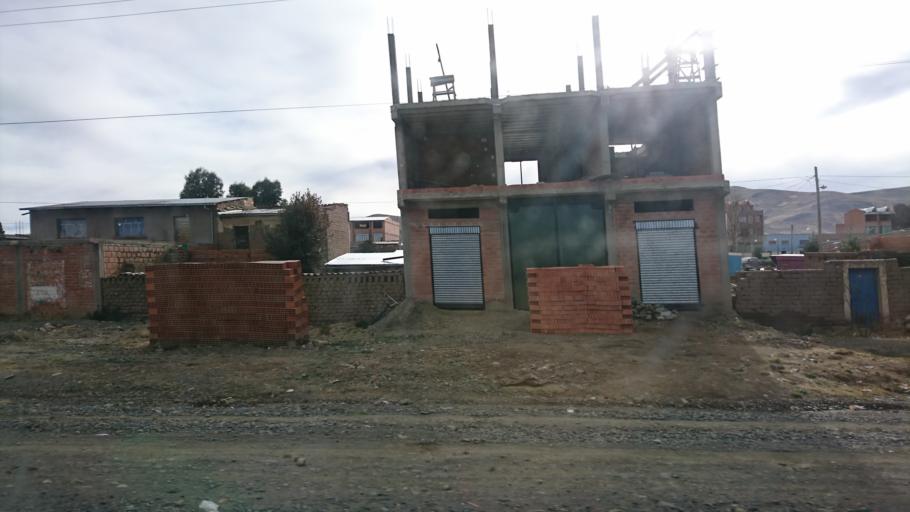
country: BO
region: La Paz
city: Batallas
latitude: -16.3775
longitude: -68.3794
